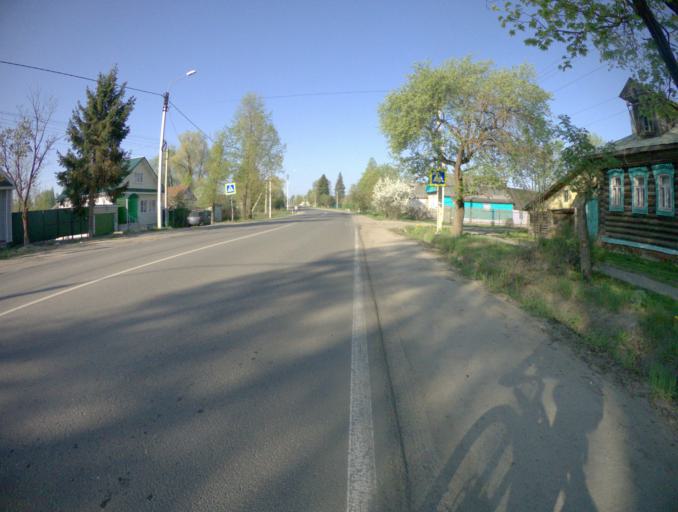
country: RU
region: Vladimir
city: Novovyazniki
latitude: 56.2144
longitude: 42.1775
